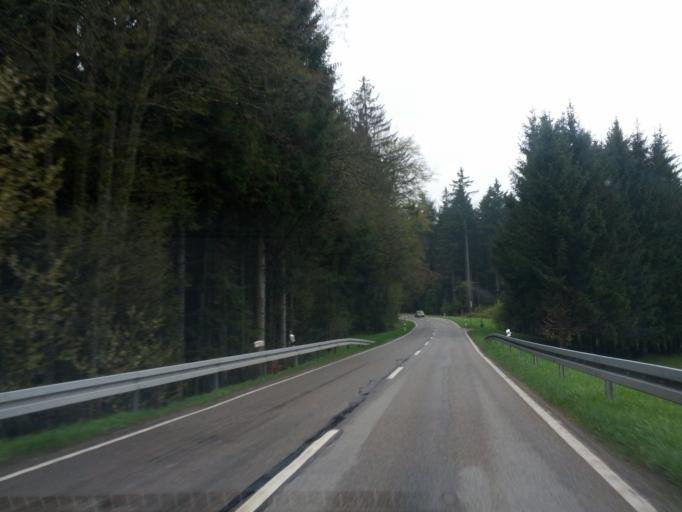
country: DE
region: Baden-Wuerttemberg
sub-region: Freiburg Region
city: Rickenbach
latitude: 47.6108
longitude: 8.0160
